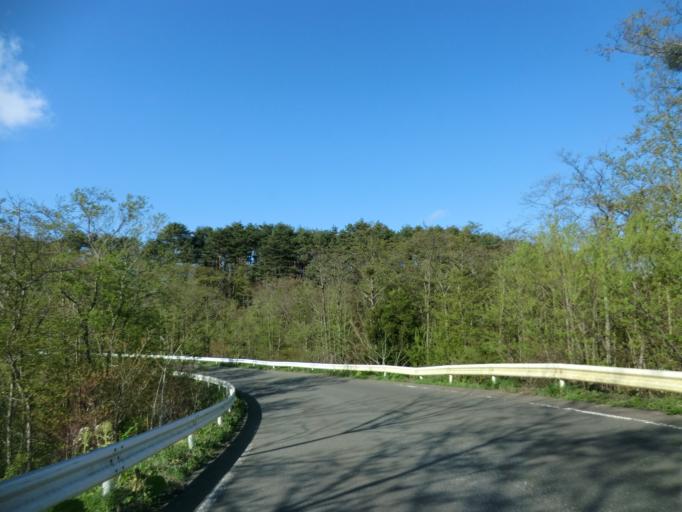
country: JP
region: Aomori
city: Mutsu
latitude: 41.2588
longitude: 141.3912
